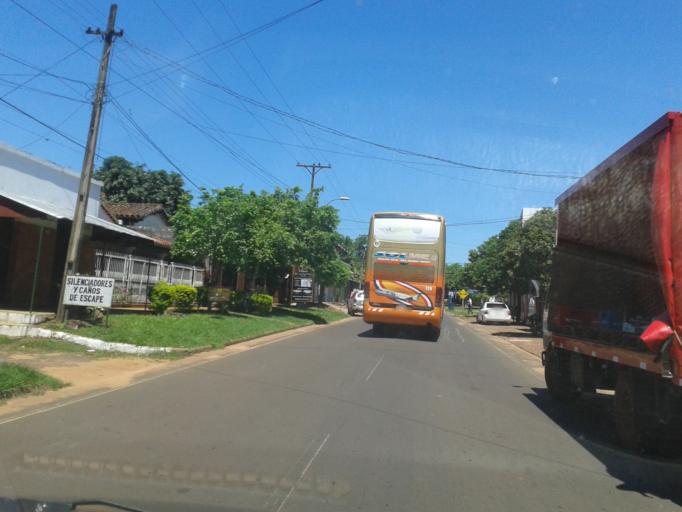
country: PY
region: Misiones
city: Santa Maria
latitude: -26.8866
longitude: -57.0187
